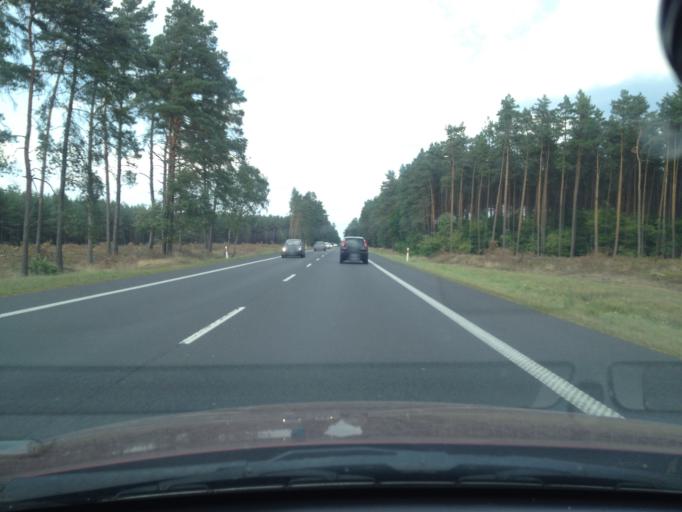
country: PL
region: West Pomeranian Voivodeship
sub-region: Powiat goleniowski
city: Goleniow
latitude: 53.6443
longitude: 14.8168
